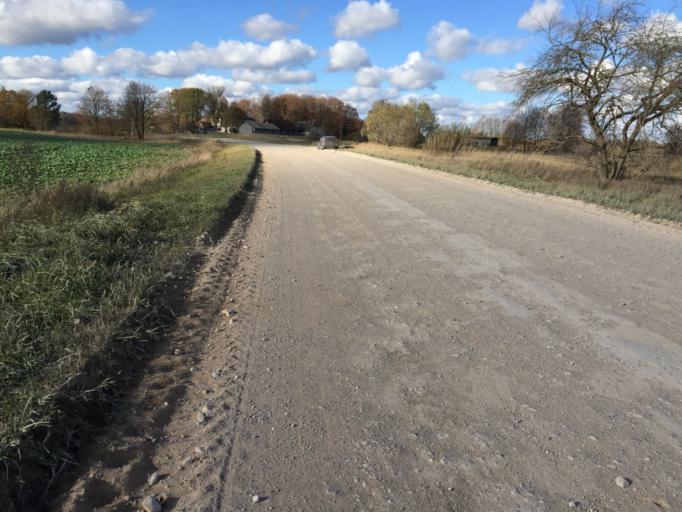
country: LV
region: Tukuma Rajons
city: Tukums
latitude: 56.9672
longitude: 22.9650
